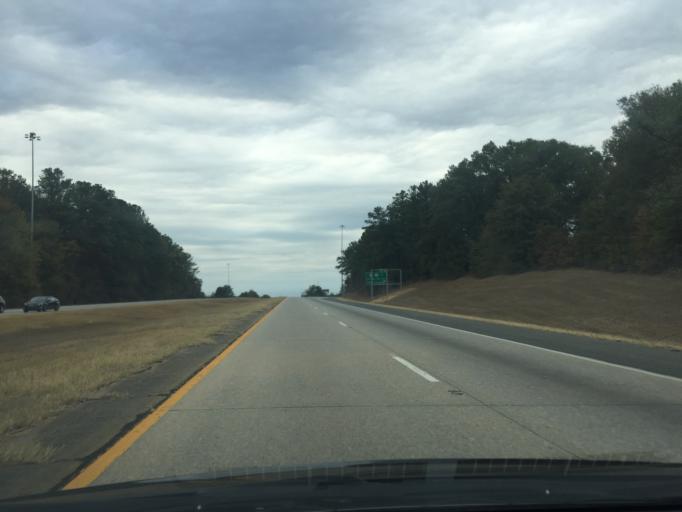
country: US
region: Georgia
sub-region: Bibb County
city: Macon
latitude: 32.7943
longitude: -83.5654
